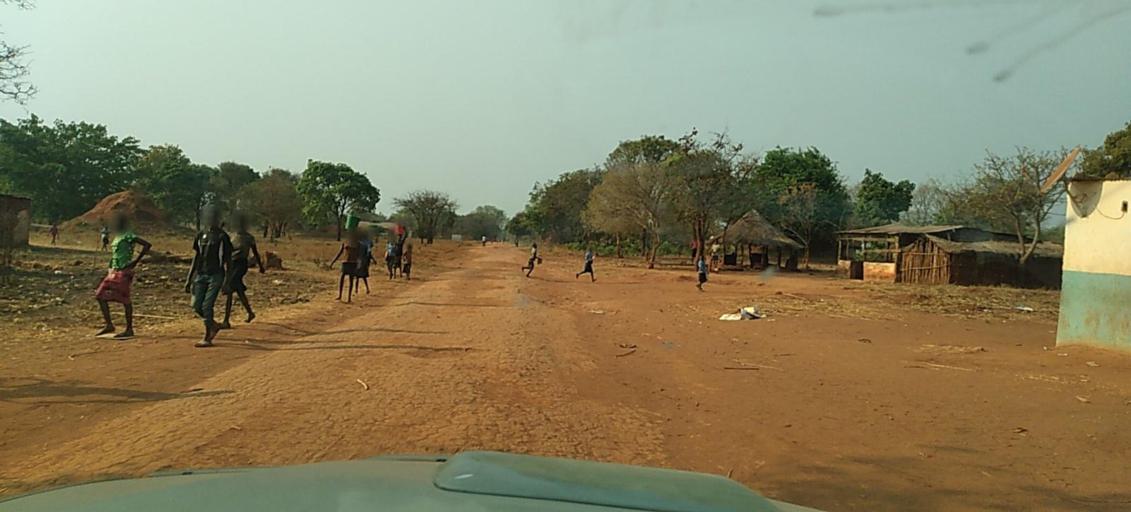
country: ZM
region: North-Western
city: Kasempa
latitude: -13.3022
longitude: 26.5538
